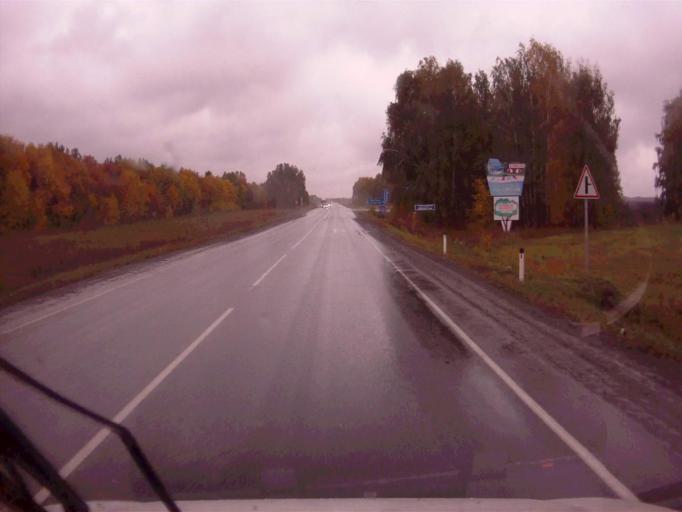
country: RU
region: Chelyabinsk
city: Roshchino
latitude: 55.3949
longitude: 61.1005
